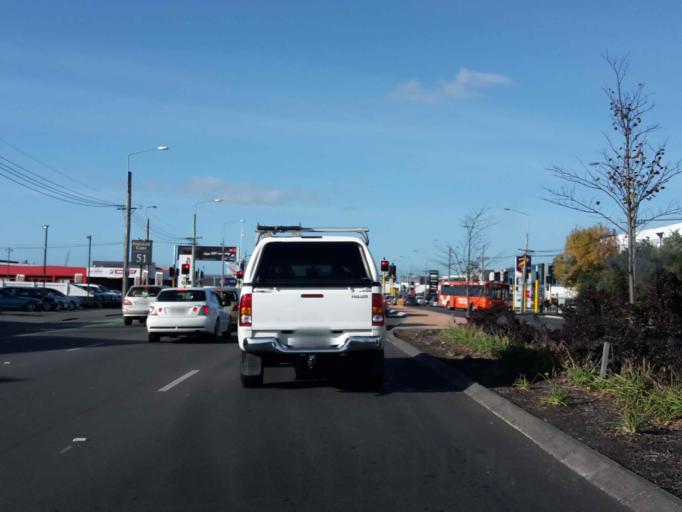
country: NZ
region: Canterbury
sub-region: Christchurch City
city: Christchurch
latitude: -43.5399
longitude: 172.6206
